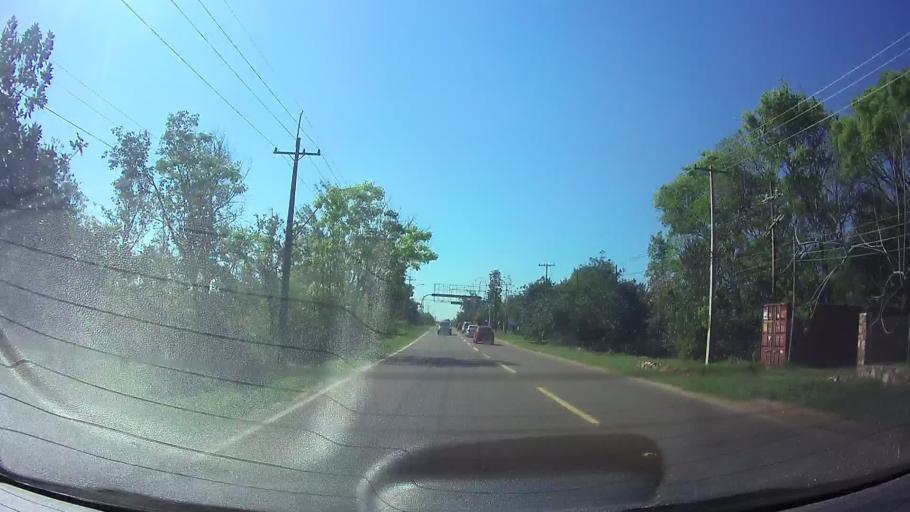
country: PY
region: Central
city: Ypacarai
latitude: -25.3609
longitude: -57.2653
